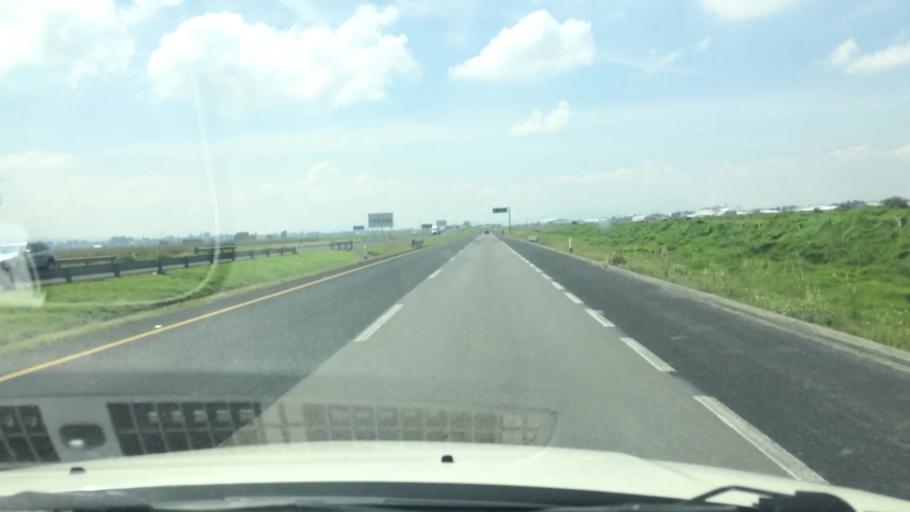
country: MX
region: Mexico
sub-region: Lerma
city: Colonia Isidro Fabela
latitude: 19.3151
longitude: -99.5221
